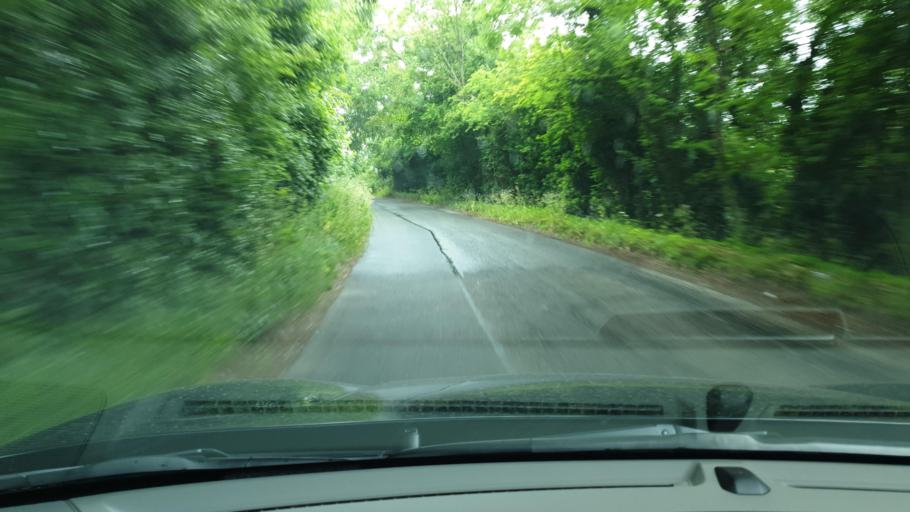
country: IE
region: Leinster
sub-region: Fingal County
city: Blanchardstown
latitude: 53.4152
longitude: -6.3958
